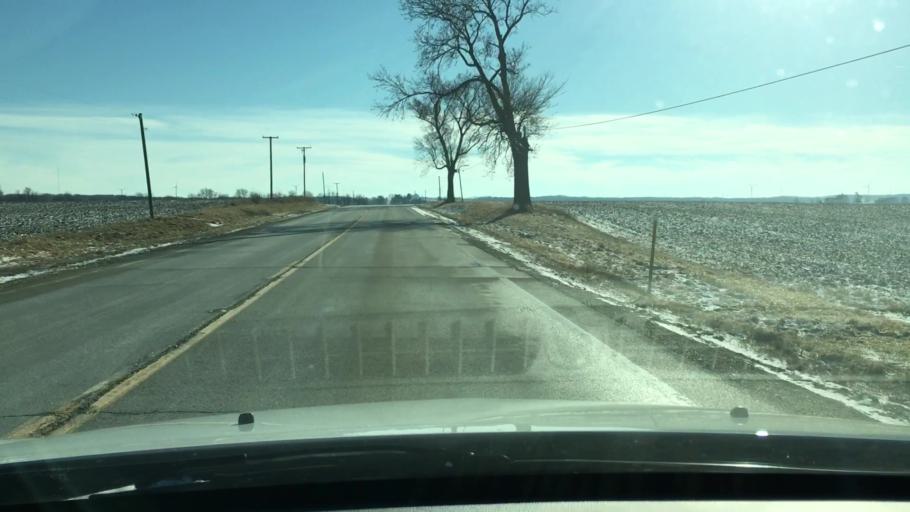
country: US
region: Illinois
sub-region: Ogle County
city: Rochelle
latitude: 41.7554
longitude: -89.0837
